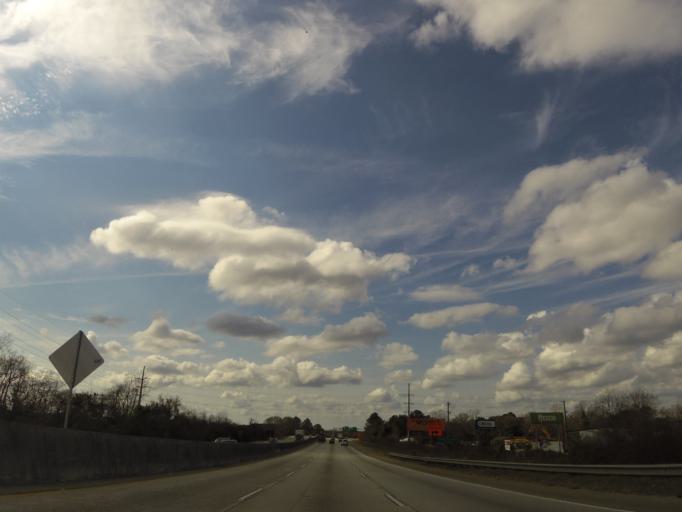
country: US
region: South Carolina
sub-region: Charleston County
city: North Charleston
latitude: 32.8424
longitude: -79.9717
